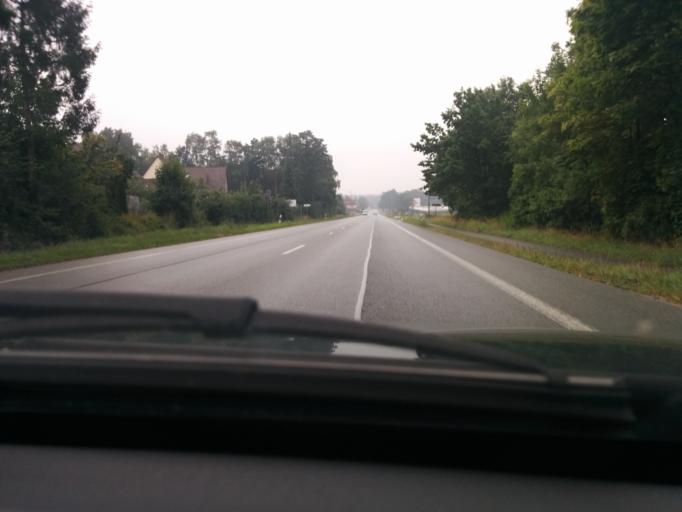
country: DE
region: North Rhine-Westphalia
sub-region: Regierungsbezirk Detmold
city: Steinhagen
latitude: 52.0375
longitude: 8.3930
